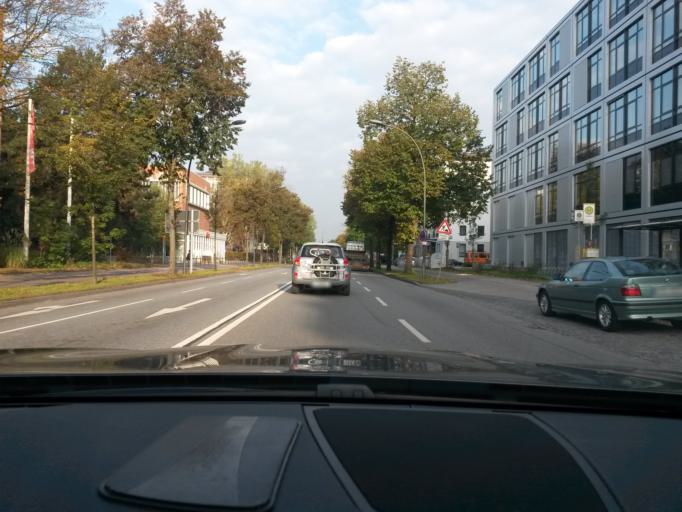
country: DE
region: Bavaria
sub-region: Lower Bavaria
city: Landshut
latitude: 48.5388
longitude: 12.1428
